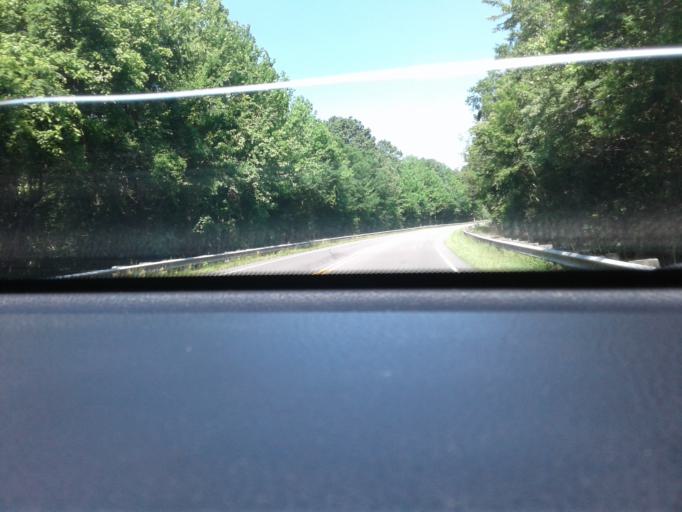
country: US
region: North Carolina
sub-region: Harnett County
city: Lillington
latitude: 35.4273
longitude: -78.8210
